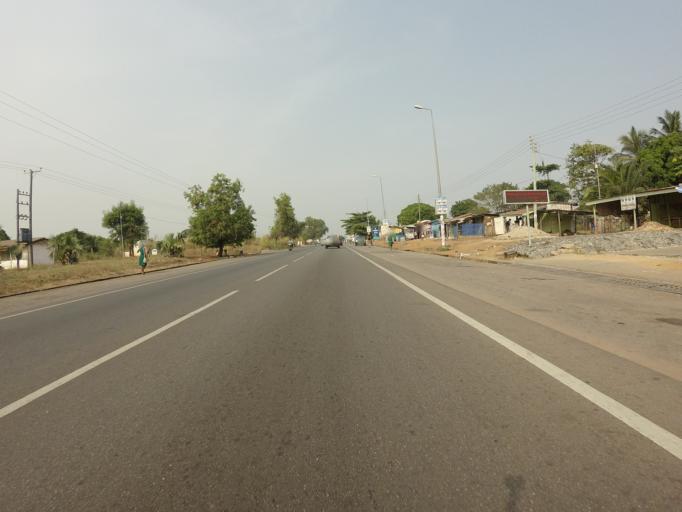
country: GH
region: Volta
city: Ho
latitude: 6.6036
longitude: 0.4833
